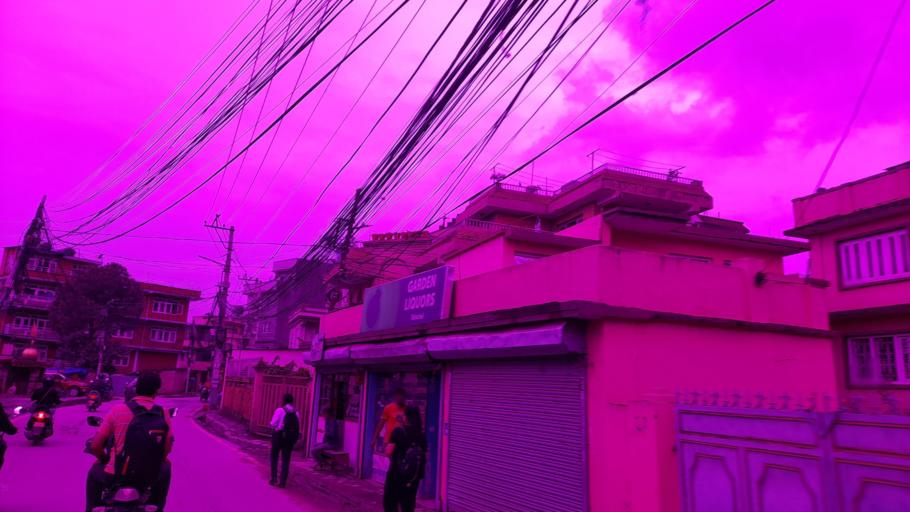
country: NP
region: Central Region
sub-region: Bagmati Zone
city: Kathmandu
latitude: 27.7010
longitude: 85.2958
